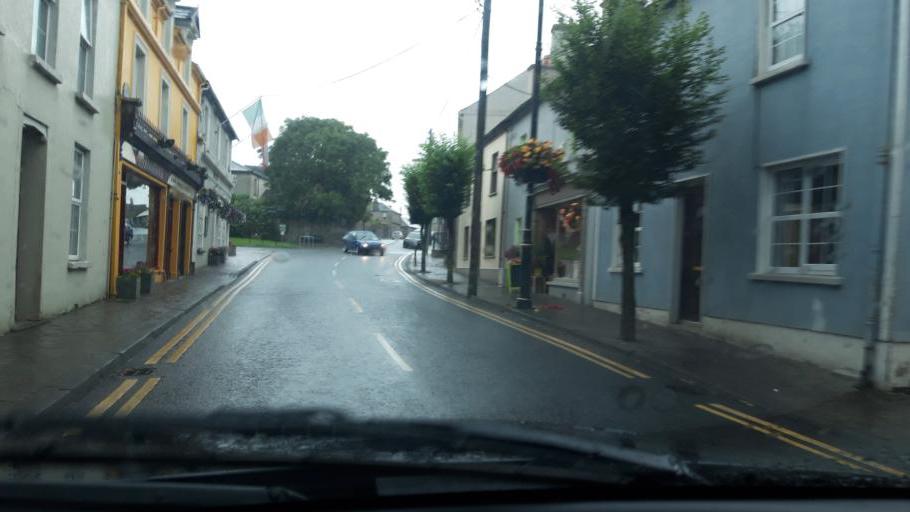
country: IE
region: Munster
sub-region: County Cork
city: Youghal
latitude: 52.1383
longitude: -7.9304
